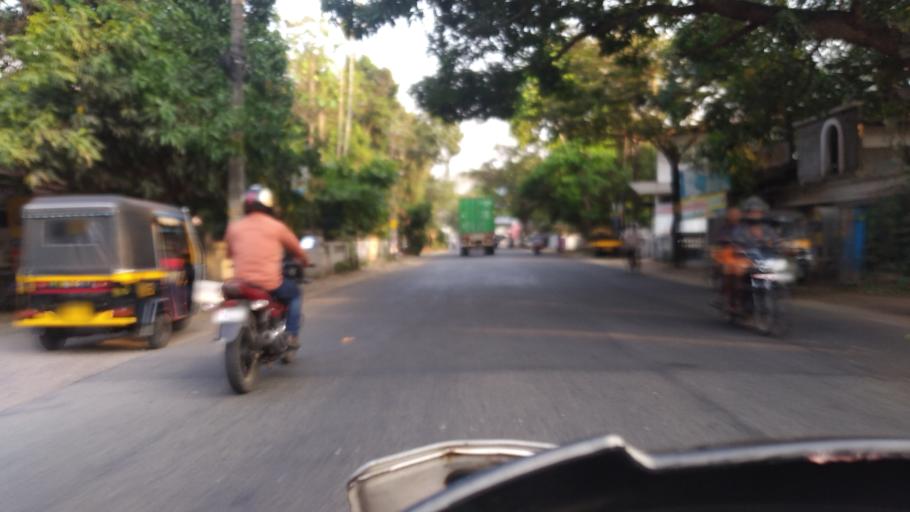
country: IN
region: Kerala
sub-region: Thrissur District
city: Irinjalakuda
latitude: 10.3343
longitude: 76.1397
